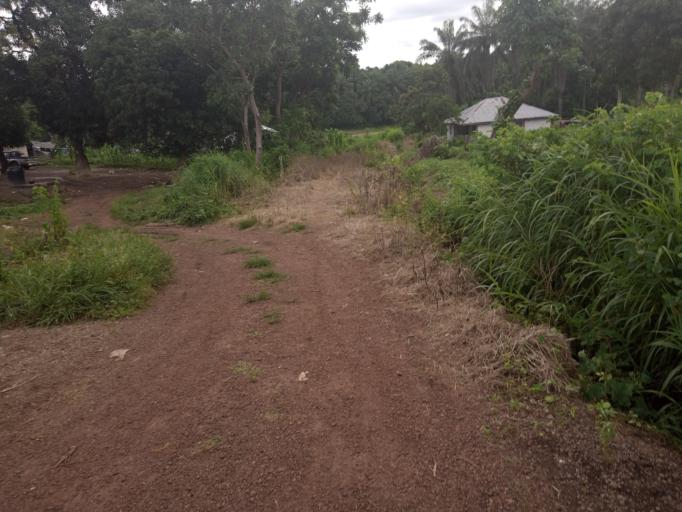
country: SL
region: Northern Province
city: Kamakwie
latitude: 9.4930
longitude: -12.2411
